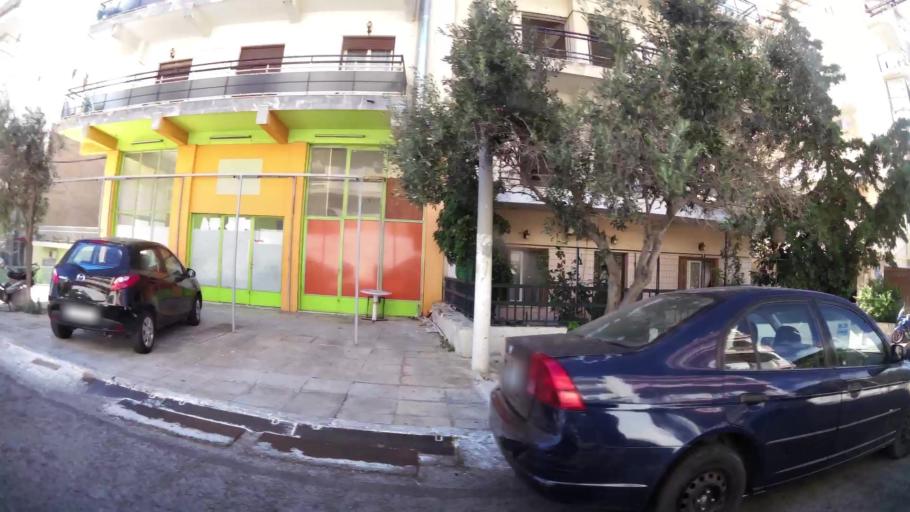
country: GR
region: Attica
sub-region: Nomos Piraios
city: Perama
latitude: 37.9680
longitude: 23.5673
